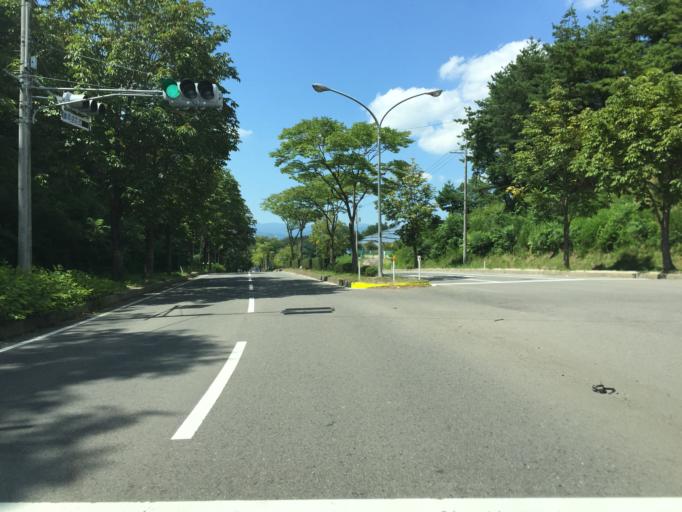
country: JP
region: Fukushima
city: Fukushima-shi
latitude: 37.7076
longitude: 140.4708
